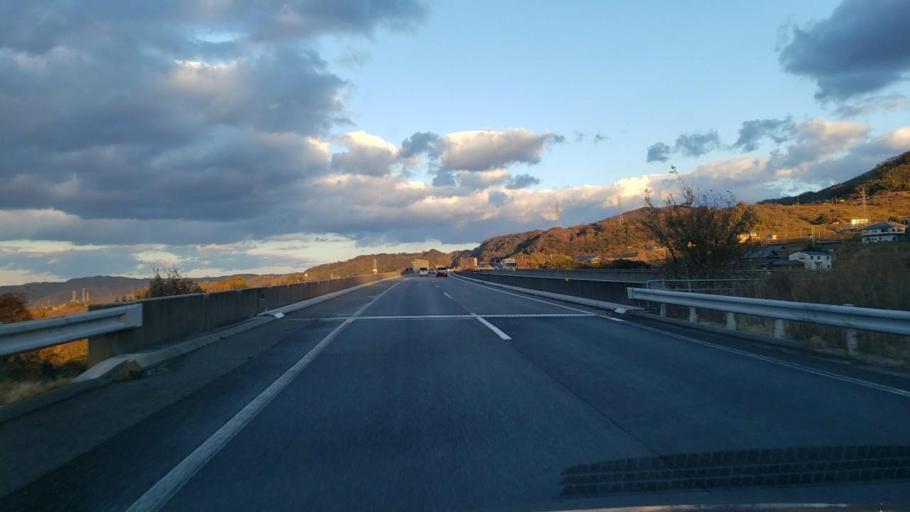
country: JP
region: Hyogo
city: Akashi
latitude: 34.5259
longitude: 134.9064
